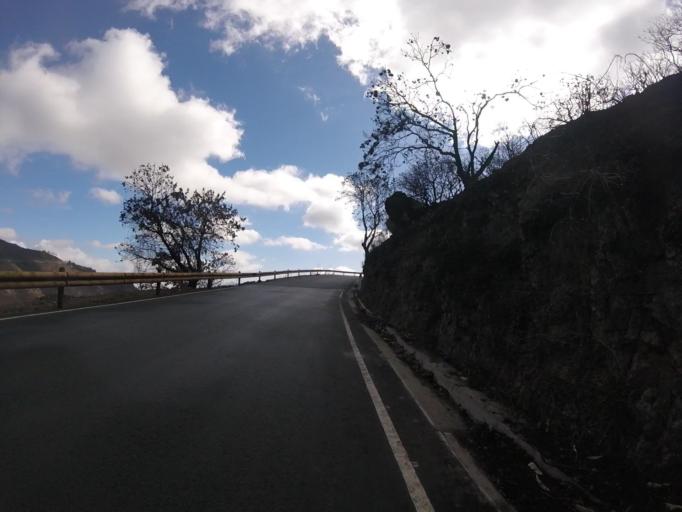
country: ES
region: Canary Islands
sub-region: Provincia de Las Palmas
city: Tejeda
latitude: 28.0043
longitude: -15.5971
